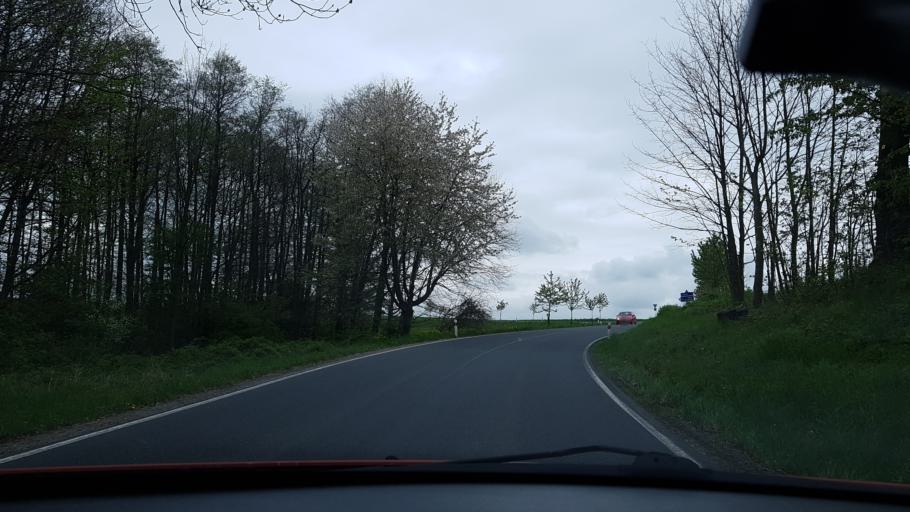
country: CZ
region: Olomoucky
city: Mikulovice
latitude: 50.3072
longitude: 17.3180
